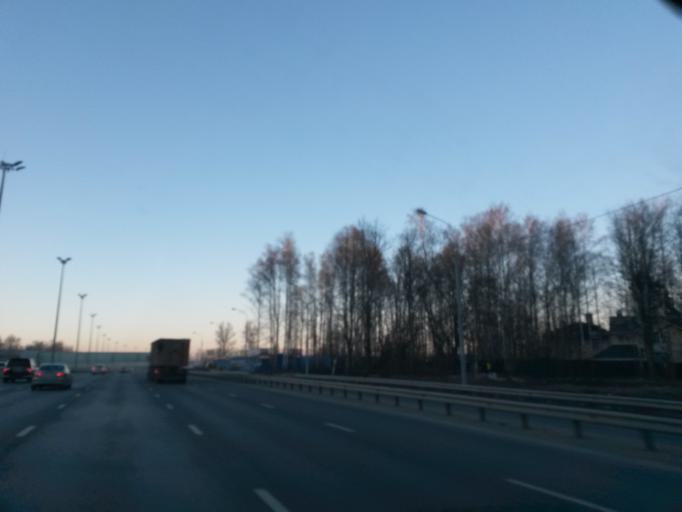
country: RU
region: Moskovskaya
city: Bolshevo
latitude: 55.9413
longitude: 37.8131
